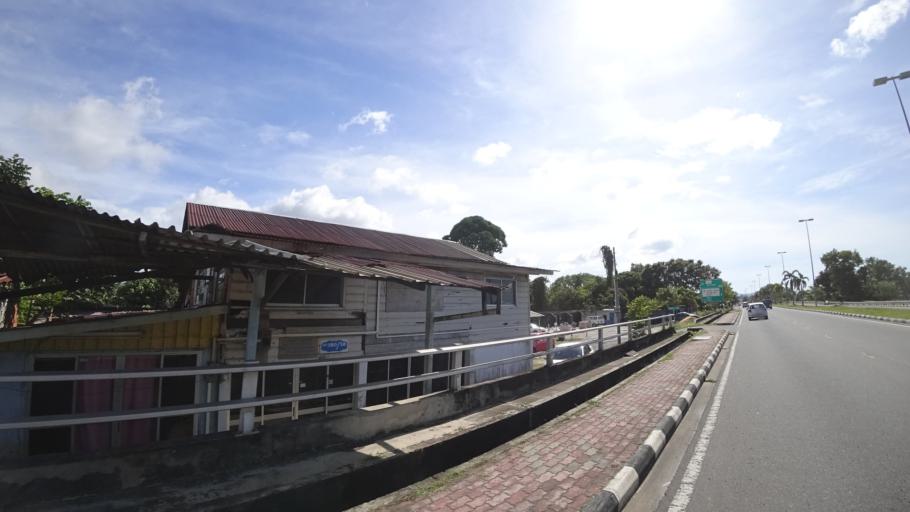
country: BN
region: Brunei and Muara
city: Bandar Seri Begawan
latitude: 4.9463
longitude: 114.9564
